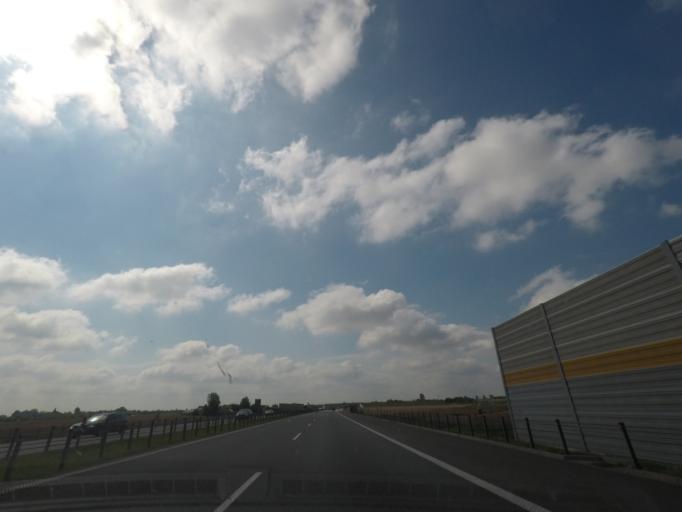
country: PL
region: Kujawsko-Pomorskie
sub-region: Powiat torunski
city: Lubicz Dolny
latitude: 53.0793
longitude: 18.7513
